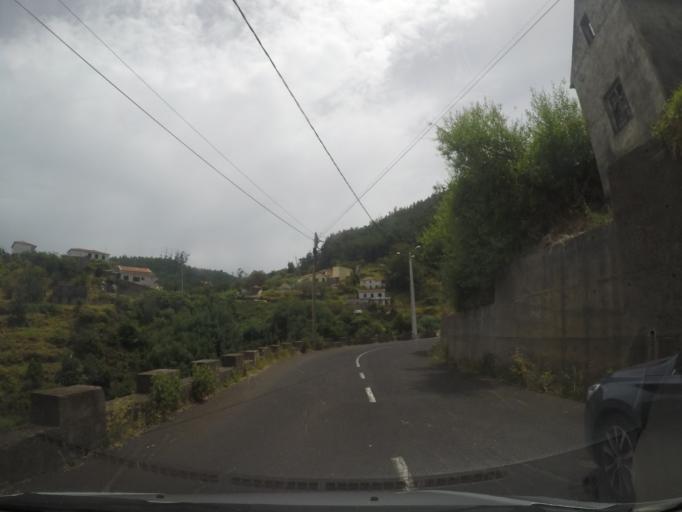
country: PT
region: Madeira
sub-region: Santa Cruz
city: Camacha
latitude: 32.6720
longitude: -16.8401
